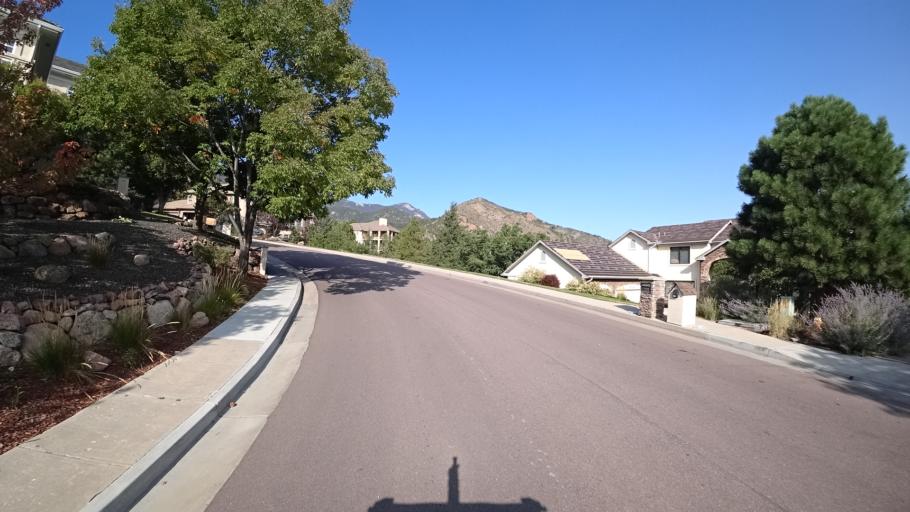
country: US
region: Colorado
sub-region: El Paso County
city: Manitou Springs
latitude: 38.8191
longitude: -104.8799
